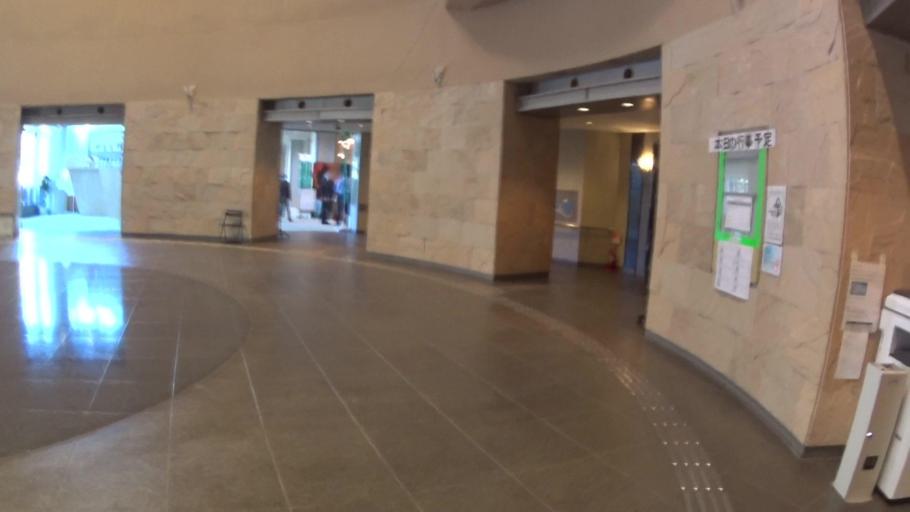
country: JP
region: Ehime
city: Kihoku-cho
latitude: 33.3683
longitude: 132.7922
